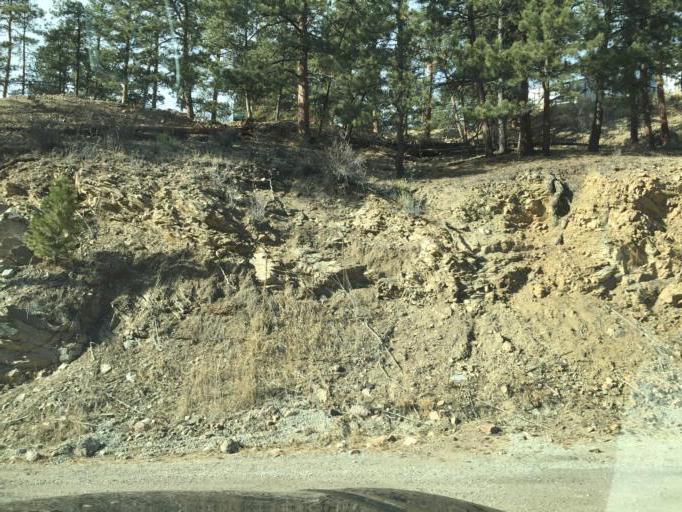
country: US
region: Colorado
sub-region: Jefferson County
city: Evergreen
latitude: 39.4083
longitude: -105.4741
